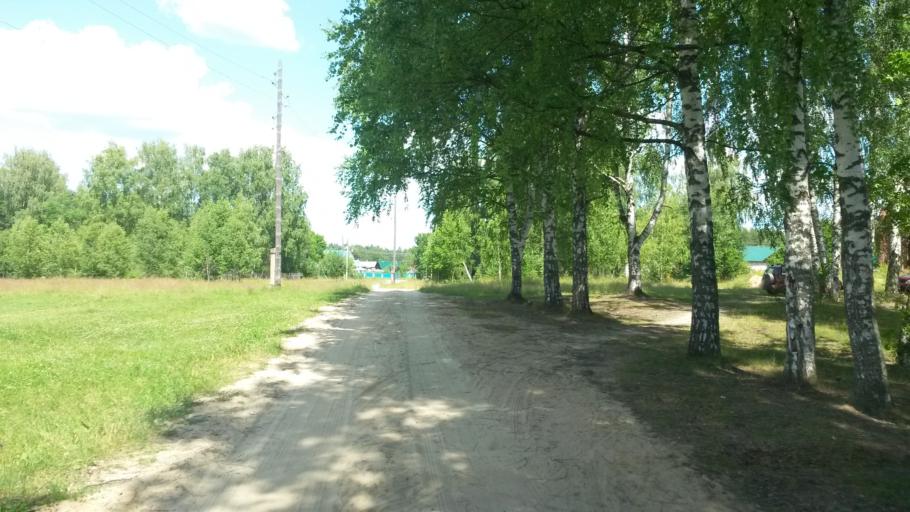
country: RU
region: Ivanovo
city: Zarechnyy
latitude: 57.4983
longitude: 42.3301
